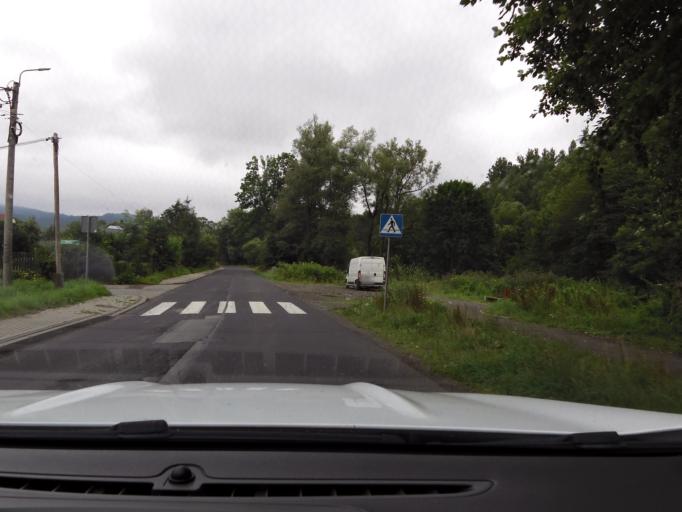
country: PL
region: Silesian Voivodeship
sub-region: Powiat zywiecki
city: Ujsoly
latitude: 49.4868
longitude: 19.1252
